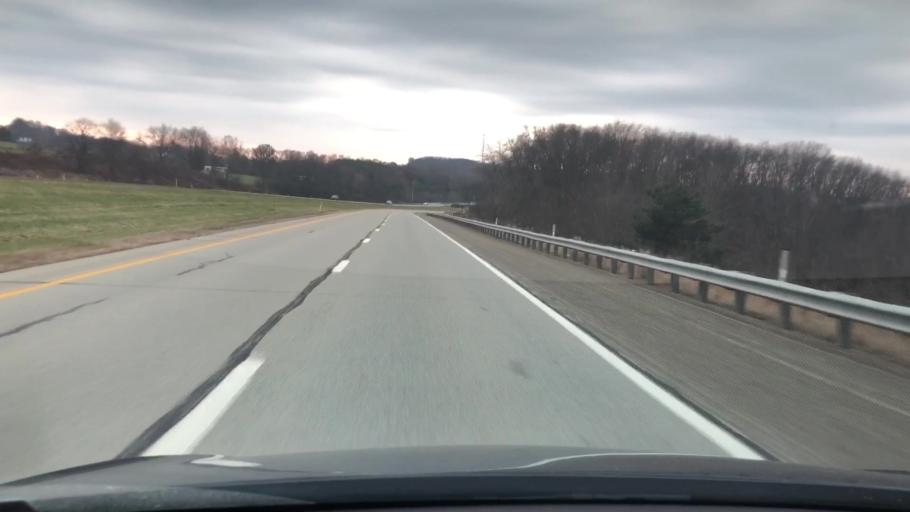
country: US
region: Pennsylvania
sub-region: Armstrong County
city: Freeport
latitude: 40.7296
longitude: -79.6669
